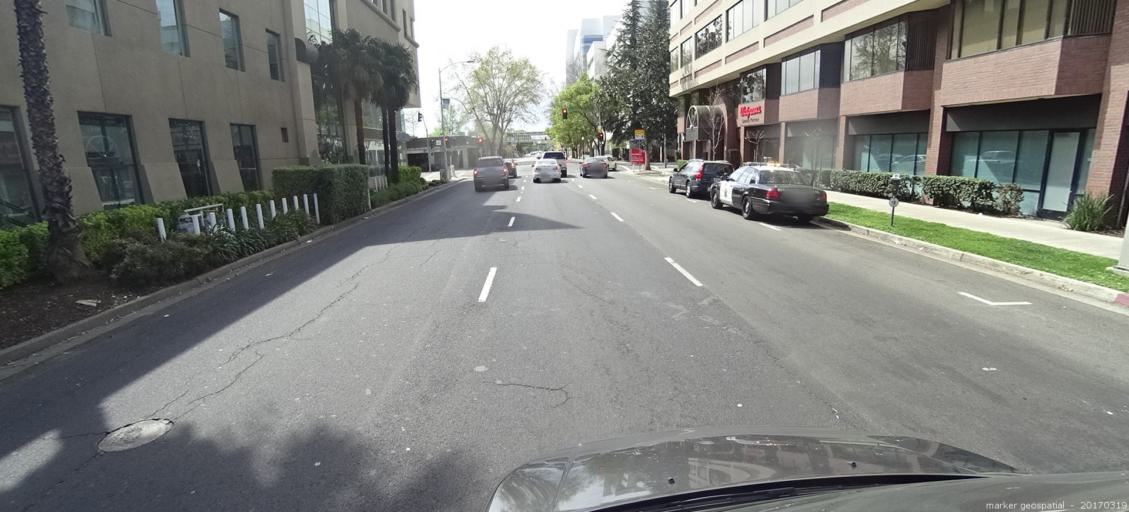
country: US
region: California
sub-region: Sacramento County
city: Sacramento
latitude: 38.5730
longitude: -121.4681
